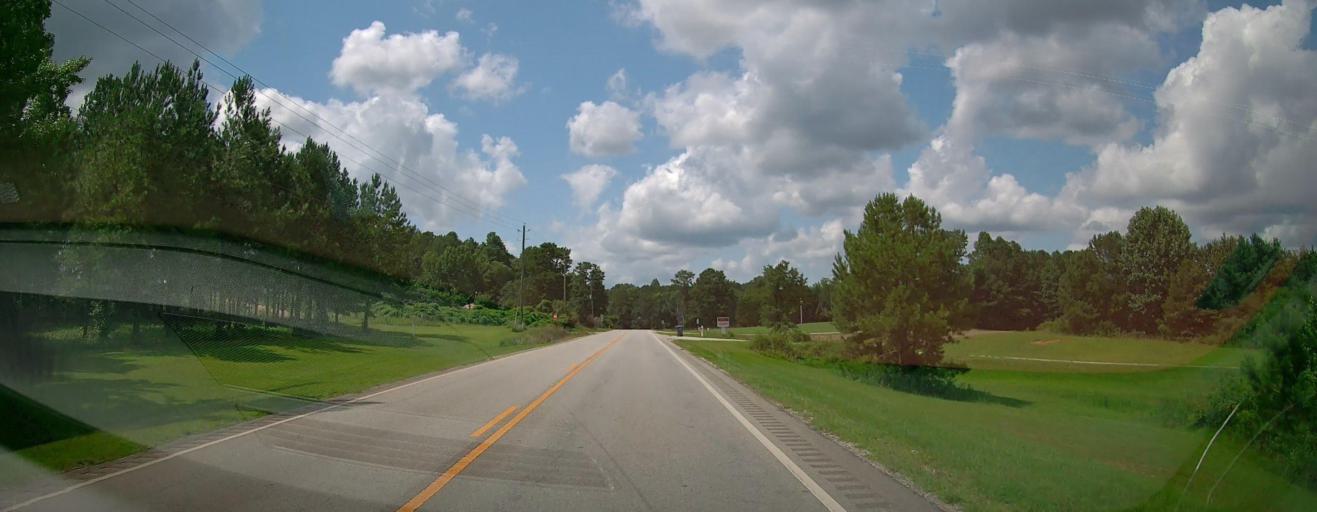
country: US
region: Georgia
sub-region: Carroll County
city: Bowdon
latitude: 33.5528
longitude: -85.4084
